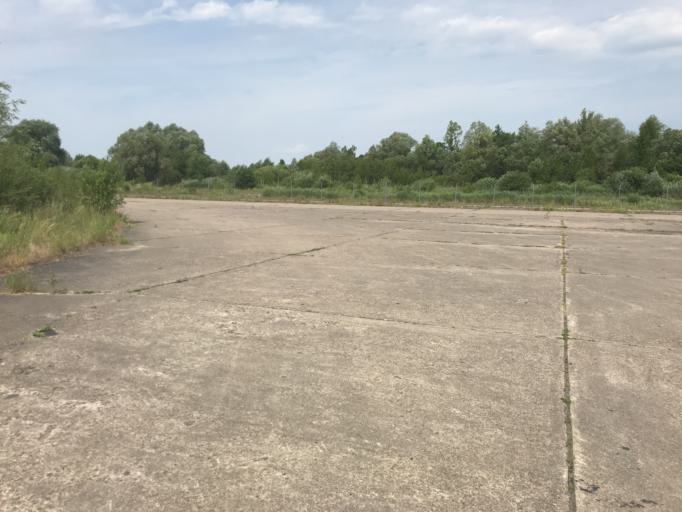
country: PL
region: West Pomeranian Voivodeship
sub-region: Powiat gryfinski
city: Chojna
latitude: 52.9420
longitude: 14.4345
